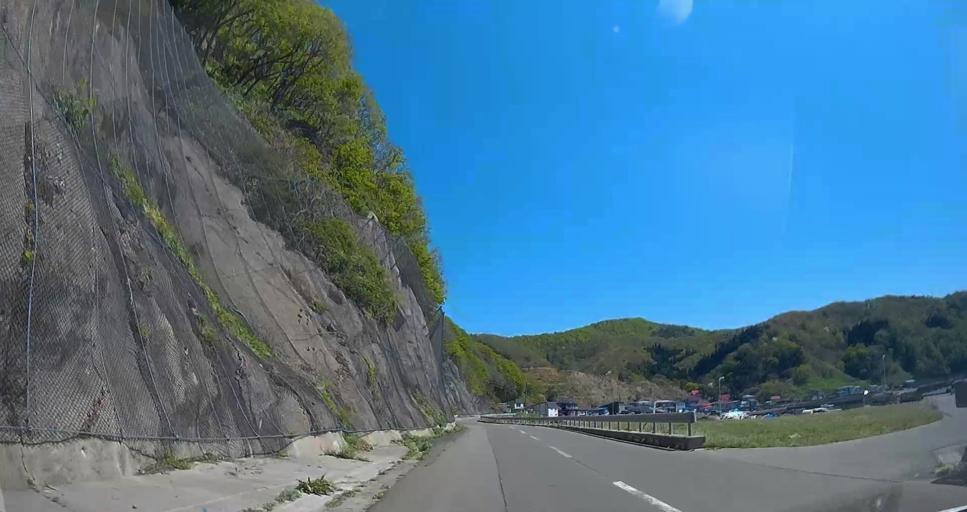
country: JP
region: Aomori
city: Aomori Shi
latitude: 41.1325
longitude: 140.7889
